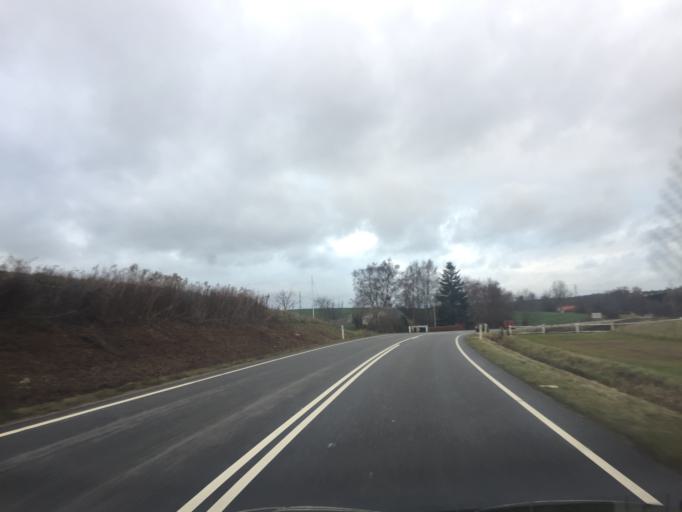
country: DK
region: Zealand
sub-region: Holbaek Kommune
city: Tollose
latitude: 55.6311
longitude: 11.7887
